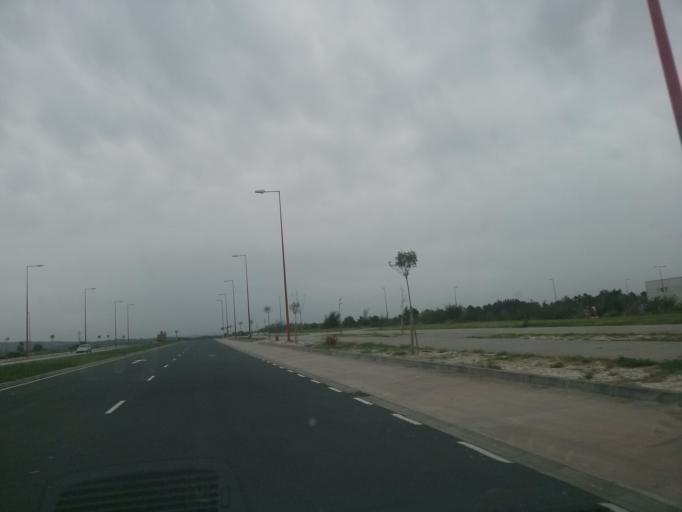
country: ES
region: Galicia
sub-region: Provincia de Lugo
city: Lugo
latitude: 43.0422
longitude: -7.5518
